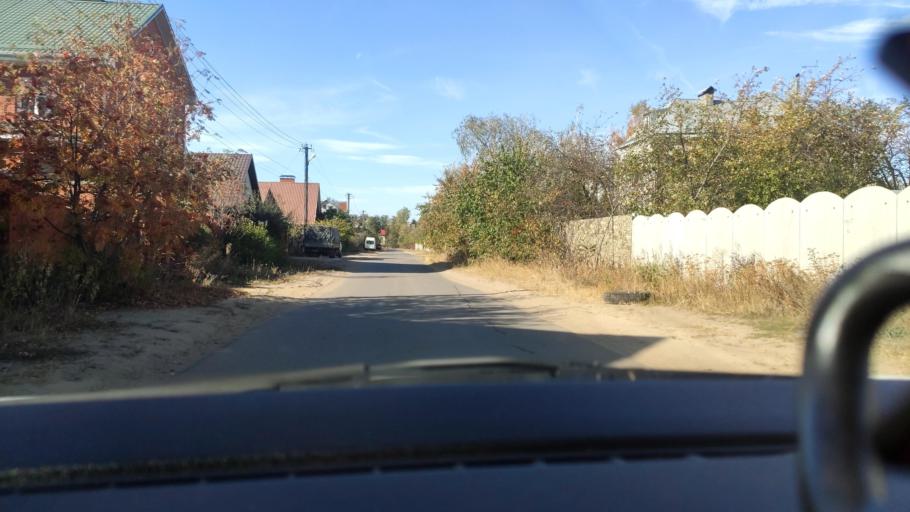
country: RU
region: Voronezj
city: Pridonskoy
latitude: 51.6399
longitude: 39.0867
